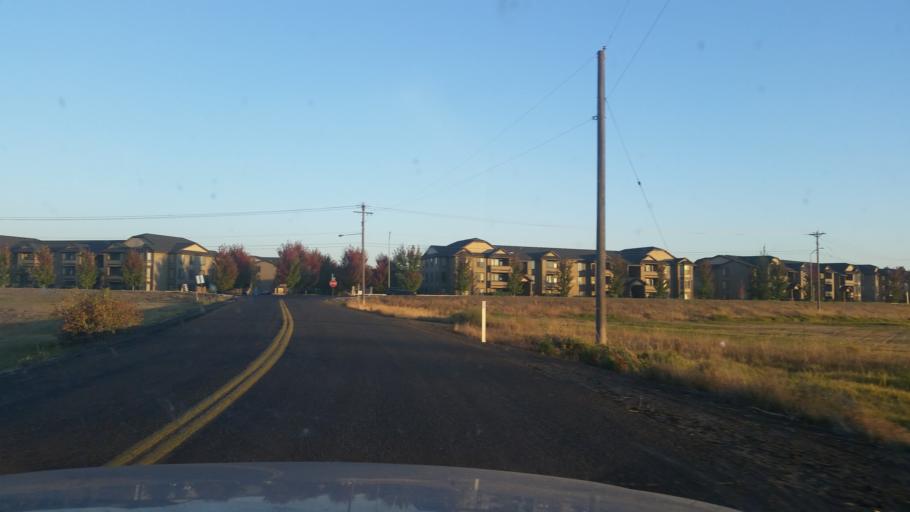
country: US
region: Washington
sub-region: Spokane County
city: Cheney
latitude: 47.5076
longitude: -117.5861
